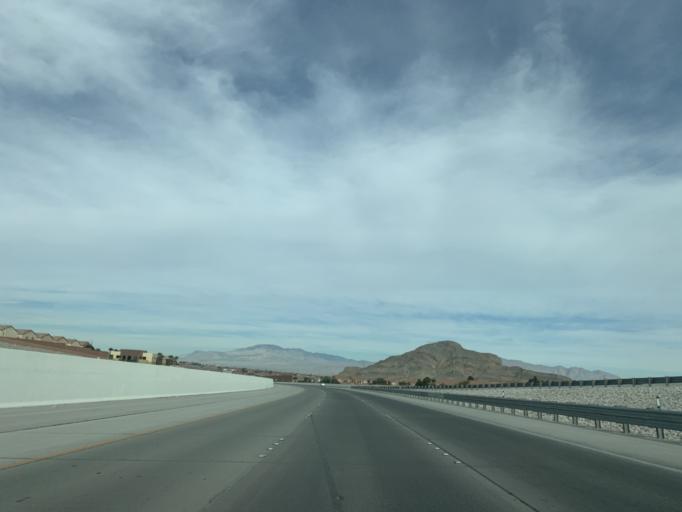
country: US
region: Nevada
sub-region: Clark County
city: Summerlin South
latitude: 36.2214
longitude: -115.3263
